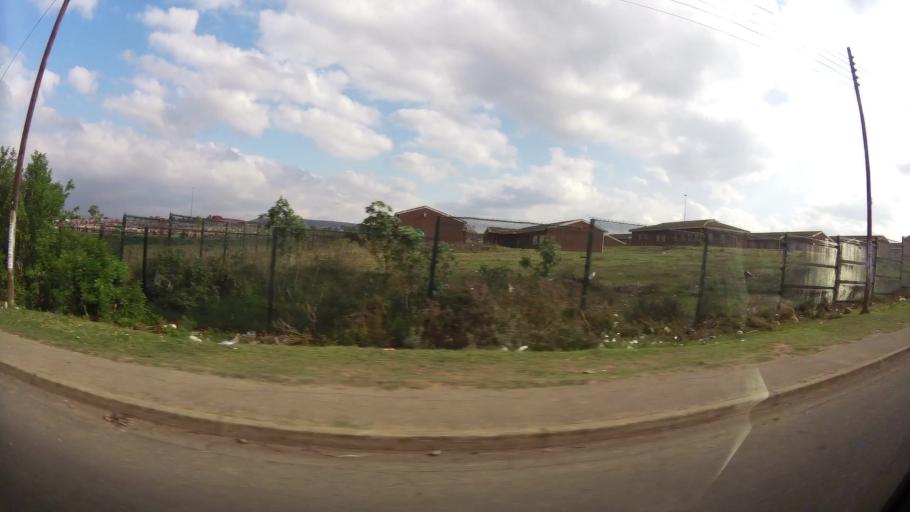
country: ZA
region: Eastern Cape
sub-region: Nelson Mandela Bay Metropolitan Municipality
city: Uitenhage
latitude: -33.7464
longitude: 25.3892
